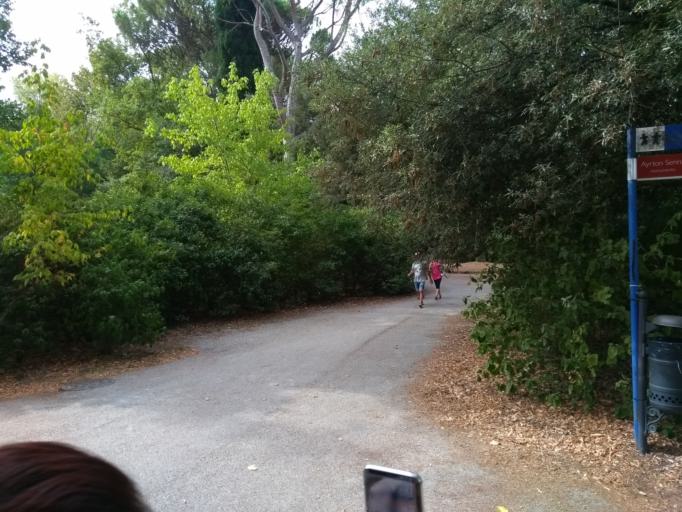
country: IT
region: Emilia-Romagna
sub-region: Provincia di Bologna
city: Imola
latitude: 44.3432
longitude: 11.7083
